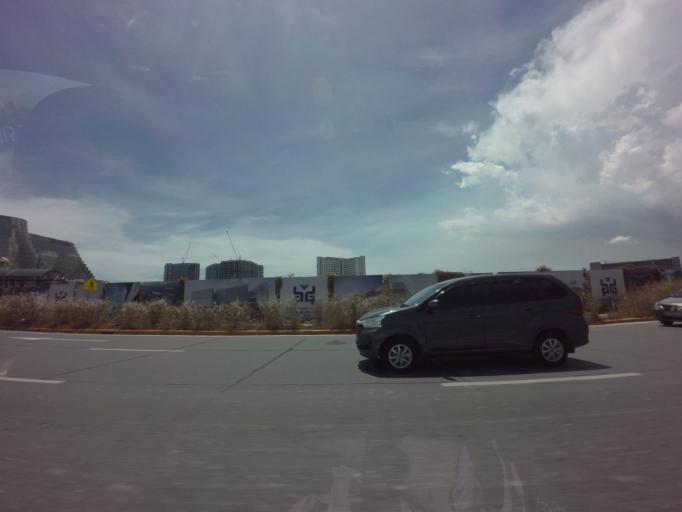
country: PH
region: Metro Manila
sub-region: Makati City
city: Makati City
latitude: 14.5162
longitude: 120.9830
